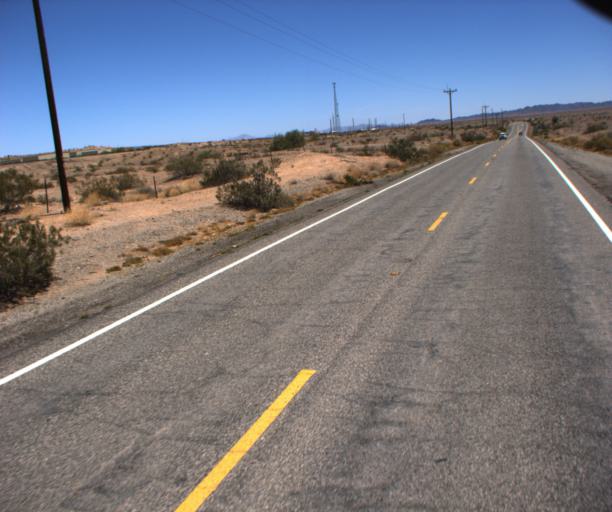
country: US
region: Arizona
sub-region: La Paz County
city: Parker
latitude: 34.0057
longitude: -114.2382
